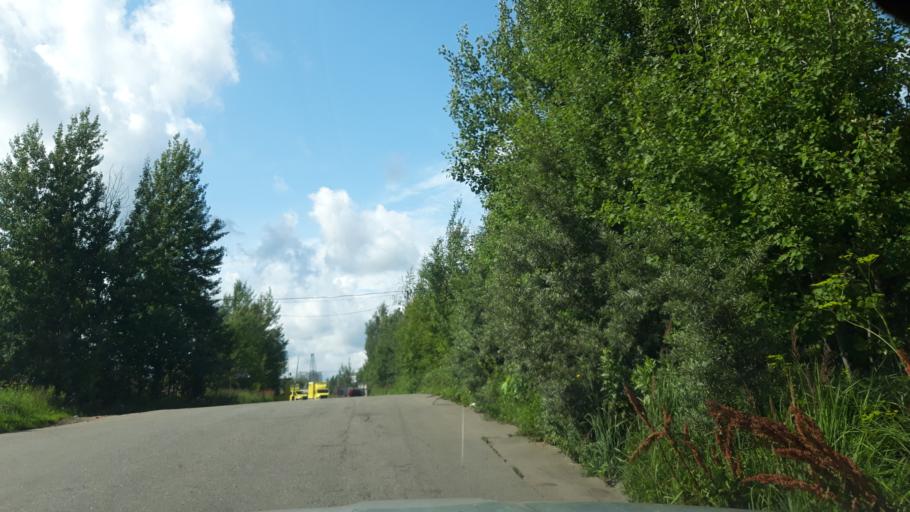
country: RU
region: Moscow
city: Zelenograd
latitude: 55.9652
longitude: 37.1702
